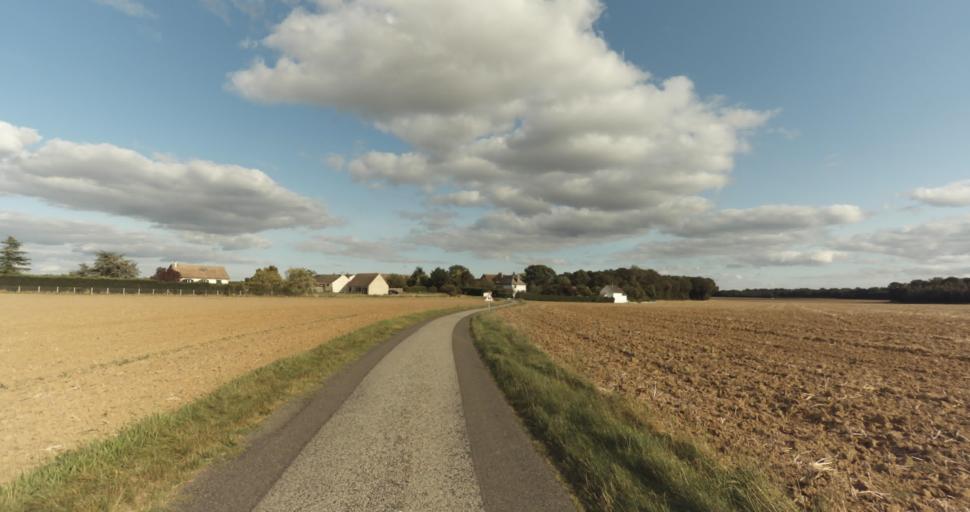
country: FR
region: Haute-Normandie
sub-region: Departement de l'Eure
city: La Couture-Boussey
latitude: 48.9042
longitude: 1.3315
